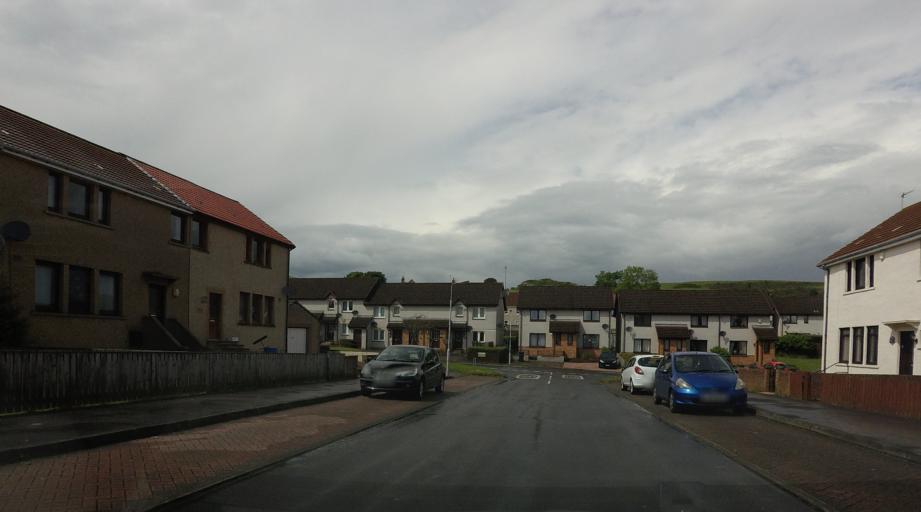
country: GB
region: Scotland
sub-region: Fife
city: Ballingry
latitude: 56.1629
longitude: -3.3298
